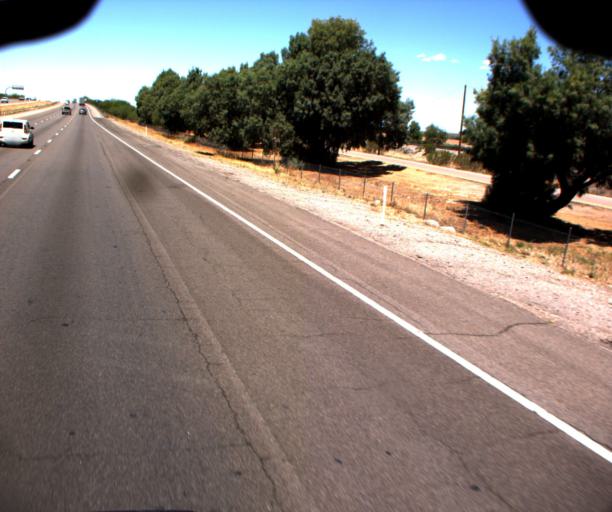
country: US
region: Arizona
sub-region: Pima County
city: Marana
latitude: 32.4055
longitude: -111.1369
